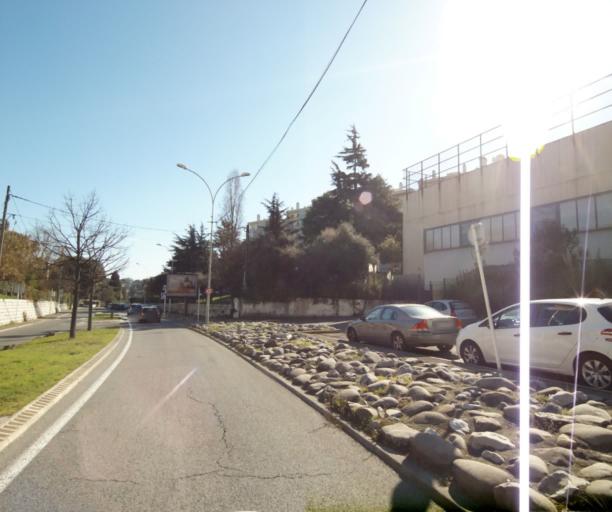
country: FR
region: Provence-Alpes-Cote d'Azur
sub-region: Departement des Alpes-Maritimes
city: Biot
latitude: 43.5933
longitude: 7.0997
